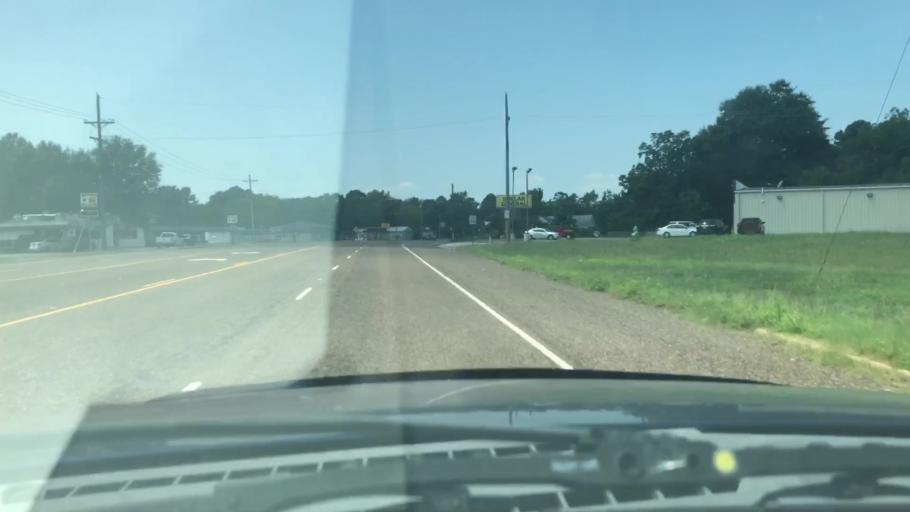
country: US
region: Texas
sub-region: Bowie County
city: Texarkana
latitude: 33.4035
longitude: -94.0659
